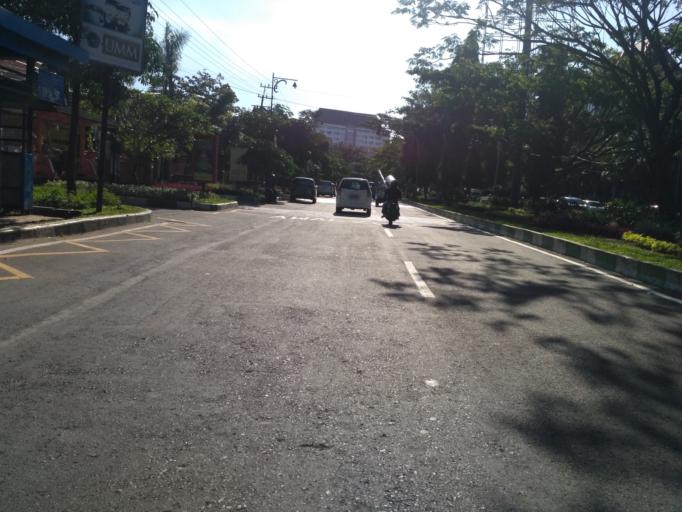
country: ID
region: East Java
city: Malang
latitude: -7.9570
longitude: 112.6173
